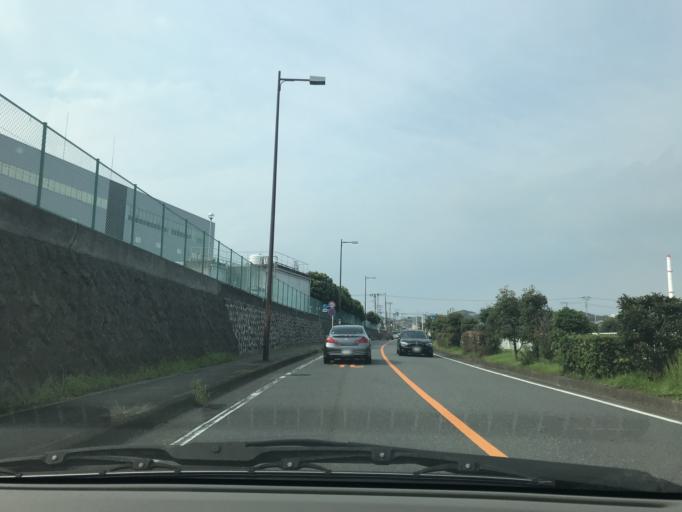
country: JP
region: Kanagawa
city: Fujisawa
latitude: 35.3399
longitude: 139.4675
